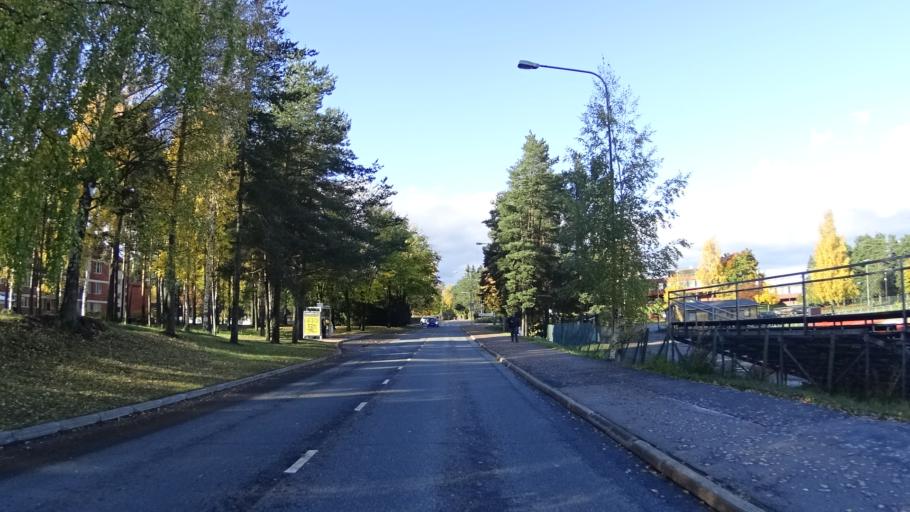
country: FI
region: Uusimaa
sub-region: Helsinki
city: Vantaa
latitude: 60.2999
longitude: 25.0537
